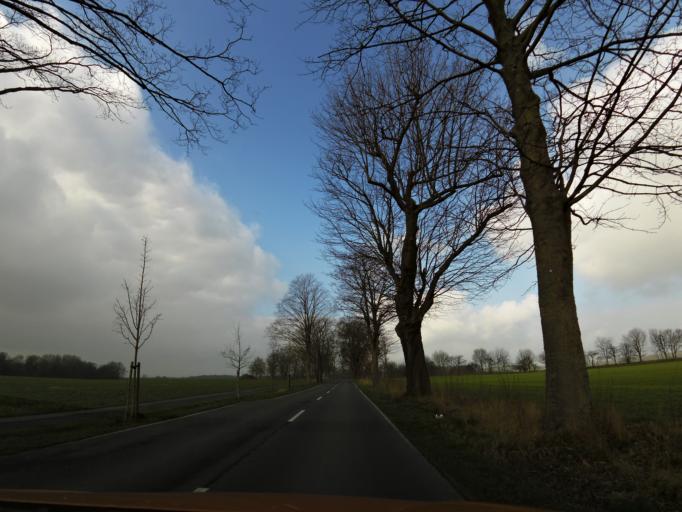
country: DE
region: Berlin
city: Wilhelmstadt
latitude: 52.5059
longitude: 13.1611
